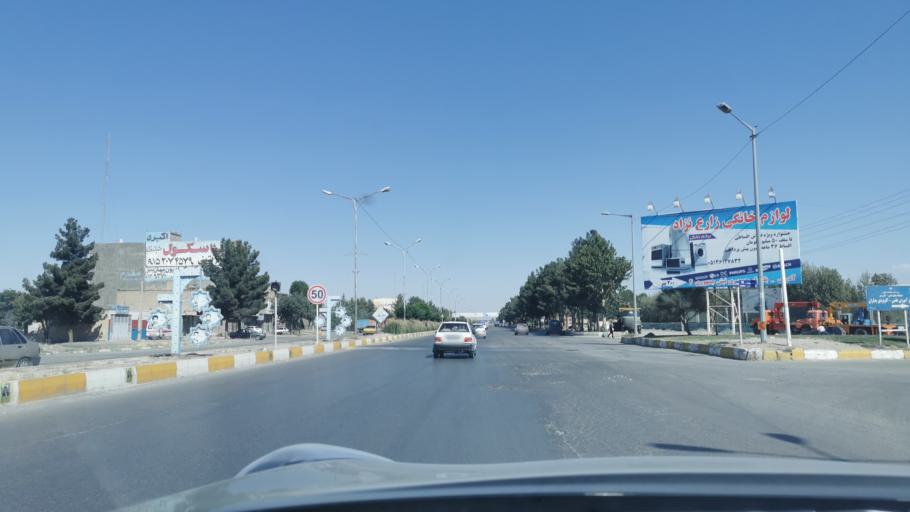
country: IR
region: Razavi Khorasan
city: Chenaran
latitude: 36.6353
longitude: 59.1282
